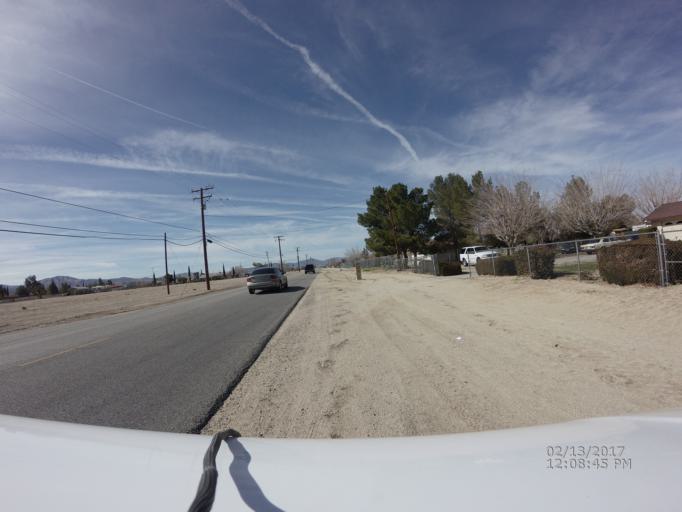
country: US
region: California
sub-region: Los Angeles County
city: Littlerock
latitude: 34.5579
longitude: -117.9654
